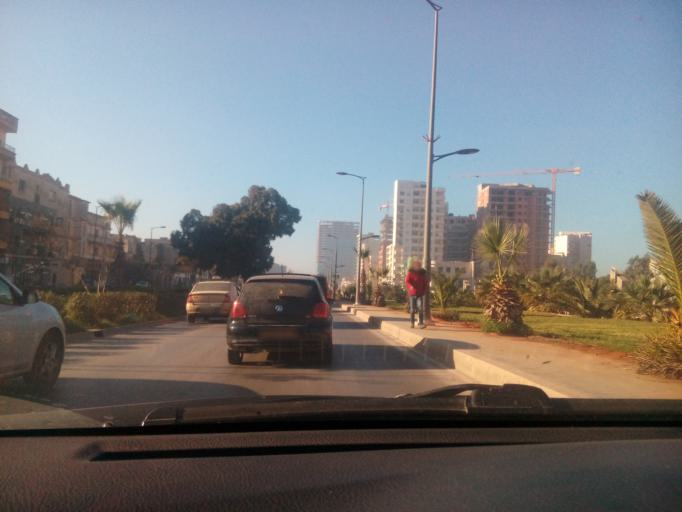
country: DZ
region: Oran
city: Bir el Djir
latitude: 35.7329
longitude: -0.5807
